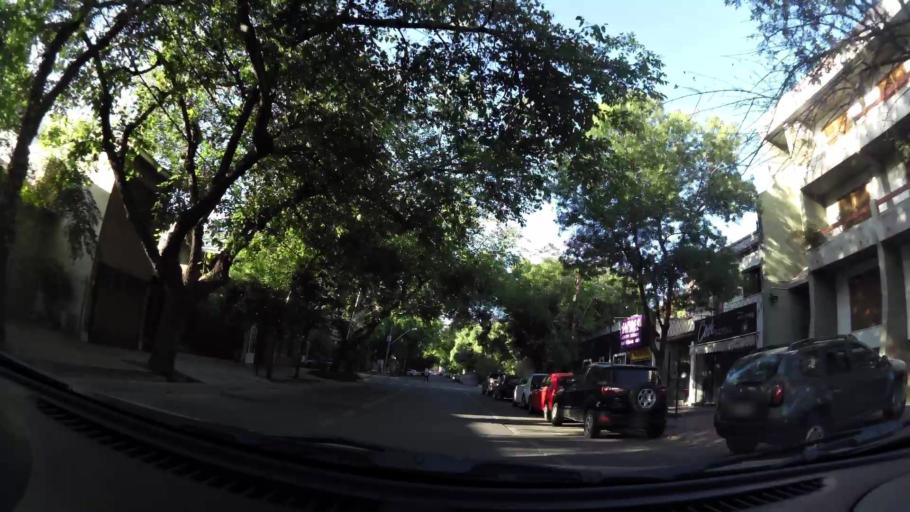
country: AR
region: Mendoza
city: Mendoza
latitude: -32.9017
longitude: -68.8437
